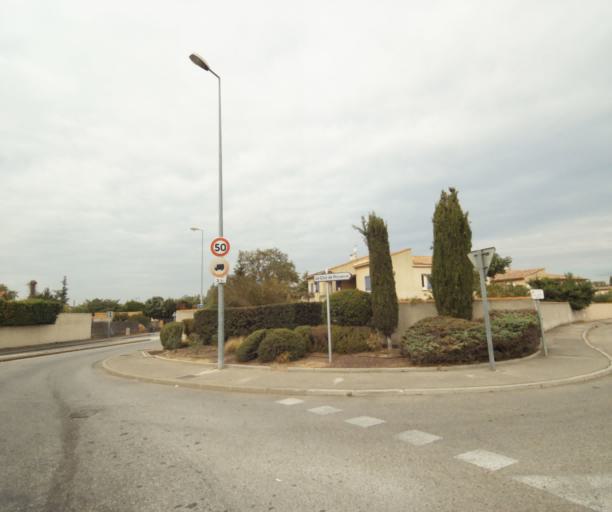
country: FR
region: Provence-Alpes-Cote d'Azur
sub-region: Departement des Bouches-du-Rhone
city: Saint-Victoret
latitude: 43.4178
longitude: 5.2593
